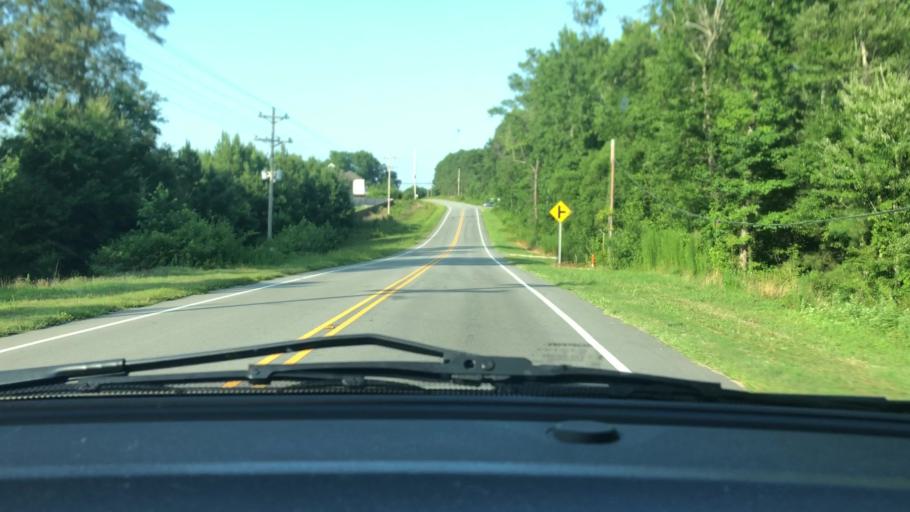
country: US
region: North Carolina
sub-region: Lee County
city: Broadway
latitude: 35.3268
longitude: -79.0622
